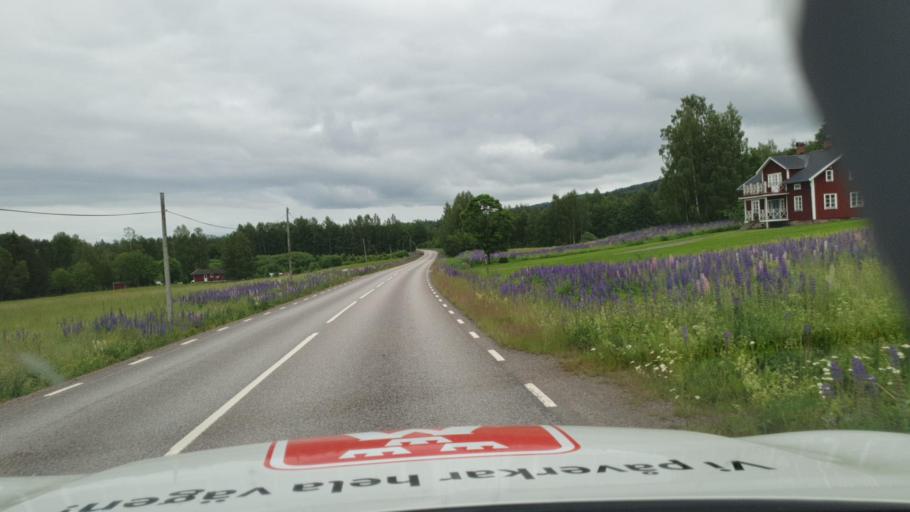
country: SE
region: Vaermland
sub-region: Sunne Kommun
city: Sunne
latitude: 59.8106
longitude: 13.0294
